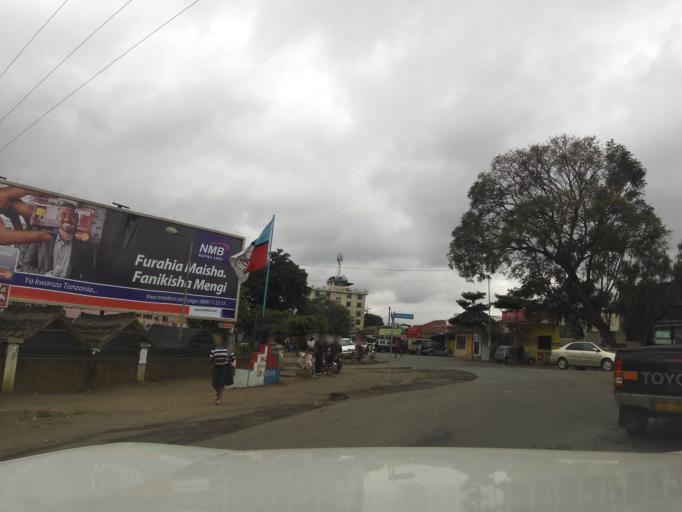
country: TZ
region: Arusha
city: Arusha
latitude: -3.3657
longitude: 36.6843
